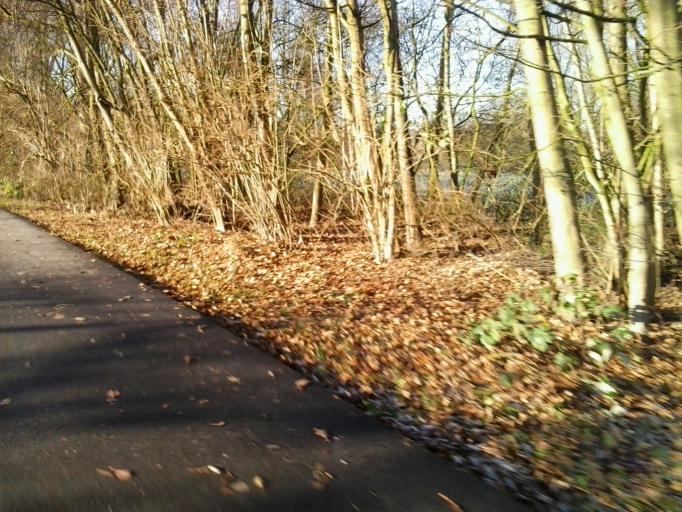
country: NL
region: South Holland
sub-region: Gemeente Lansingerland
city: Bergschenhoek
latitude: 51.9677
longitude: 4.5145
